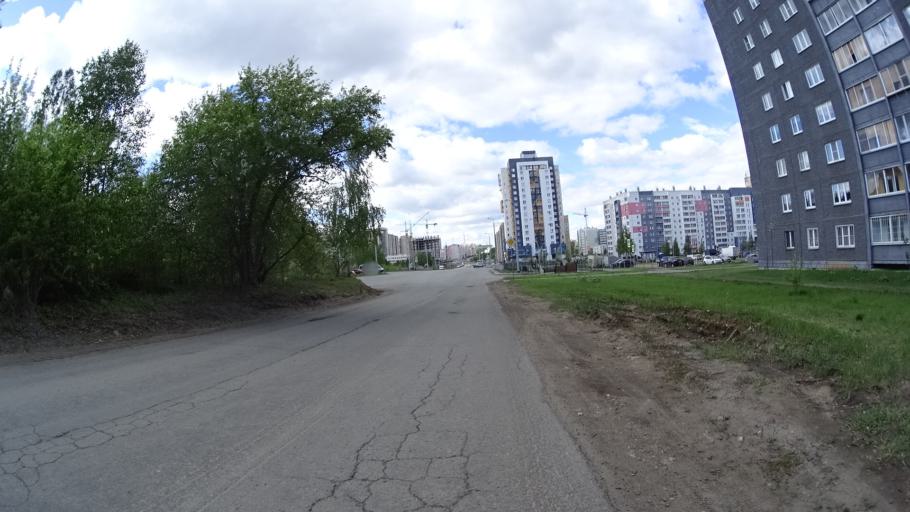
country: RU
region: Chelyabinsk
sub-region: Gorod Chelyabinsk
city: Chelyabinsk
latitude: 55.1623
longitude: 61.2858
